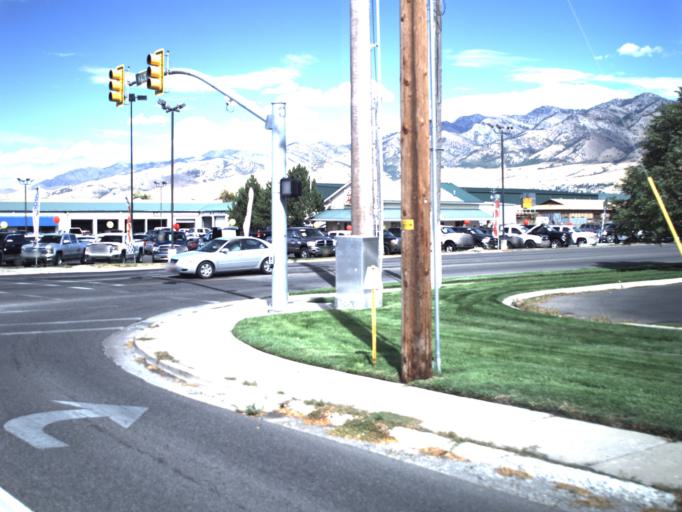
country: US
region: Utah
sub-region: Cache County
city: Logan
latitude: 41.7647
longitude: -111.8341
